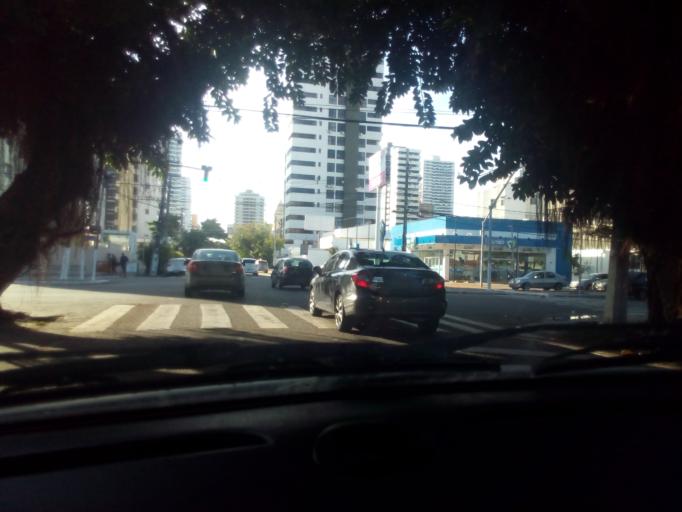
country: BR
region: Rio Grande do Norte
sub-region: Natal
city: Natal
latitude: -5.7923
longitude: -35.1986
